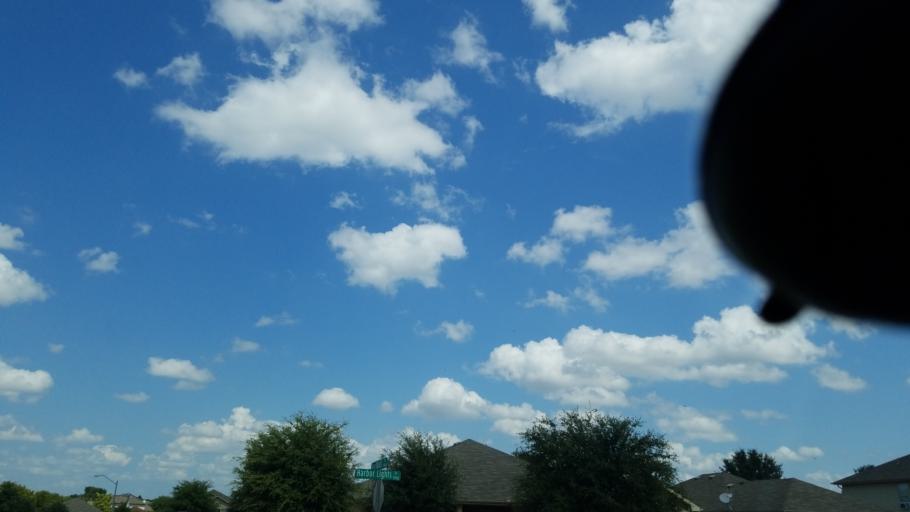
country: US
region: Texas
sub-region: Dallas County
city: Grand Prairie
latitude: 32.7196
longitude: -96.9766
